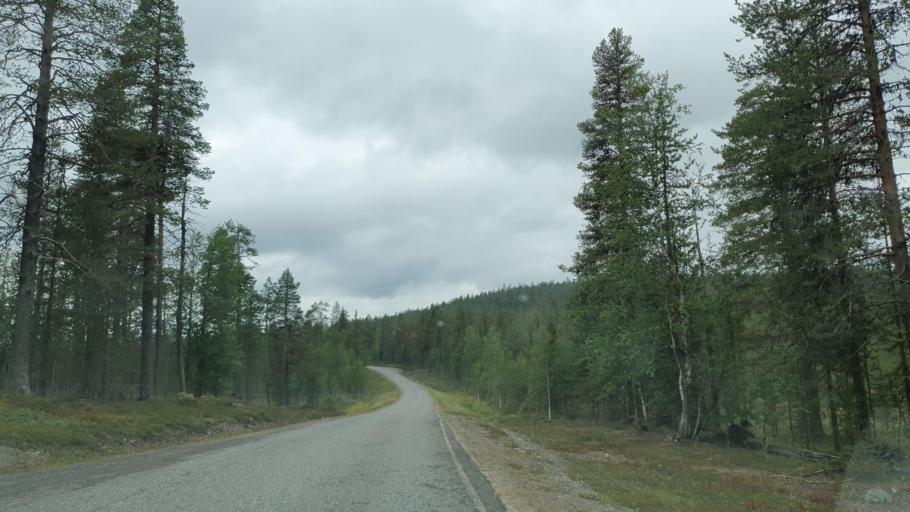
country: FI
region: Lapland
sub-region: Tunturi-Lappi
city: Muonio
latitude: 67.7297
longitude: 24.2576
